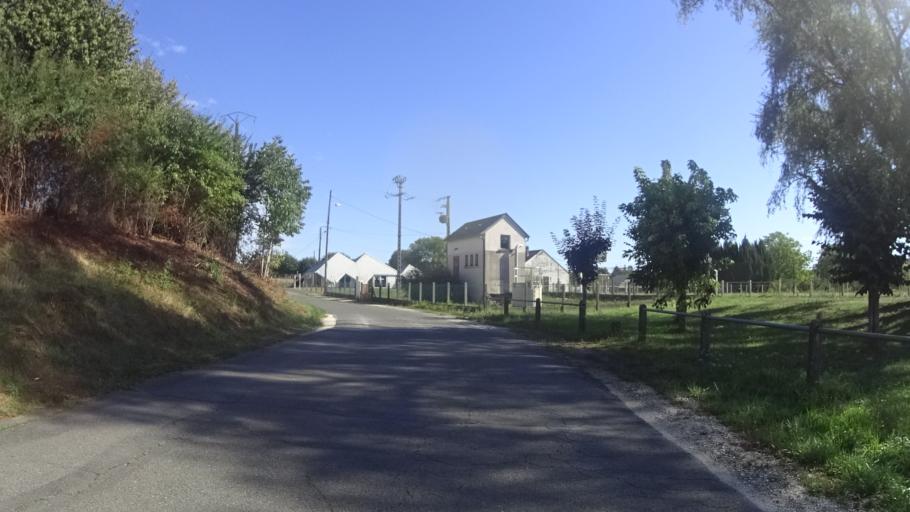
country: FR
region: Centre
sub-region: Departement du Cher
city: Saint-Satur
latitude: 47.3367
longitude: 2.8591
